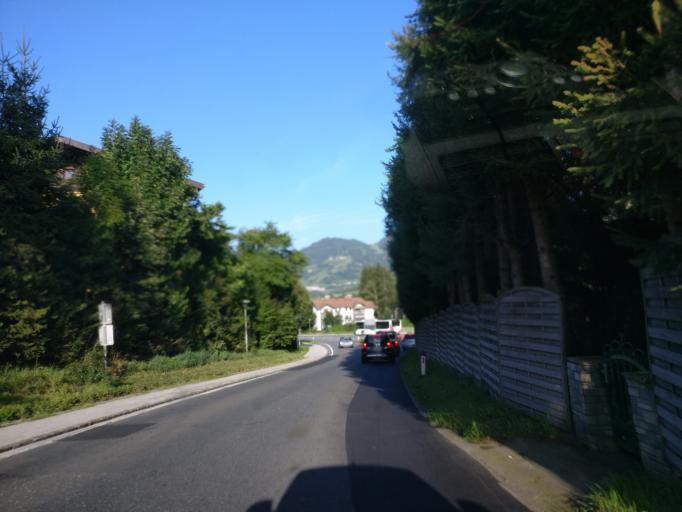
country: AT
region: Salzburg
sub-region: Politischer Bezirk Sankt Johann im Pongau
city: Schwarzach im Pongau
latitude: 47.3182
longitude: 13.1382
